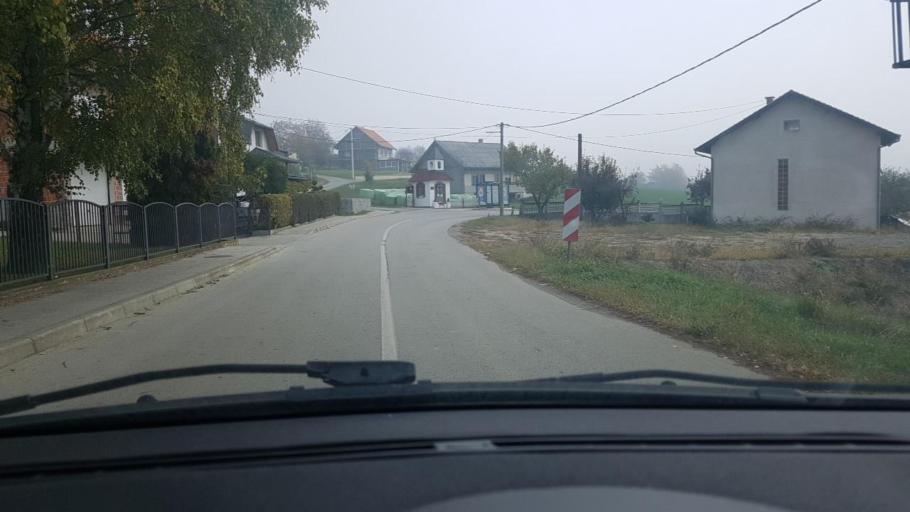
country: HR
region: Varazdinska
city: Lepoglava
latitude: 46.1513
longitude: 16.0462
